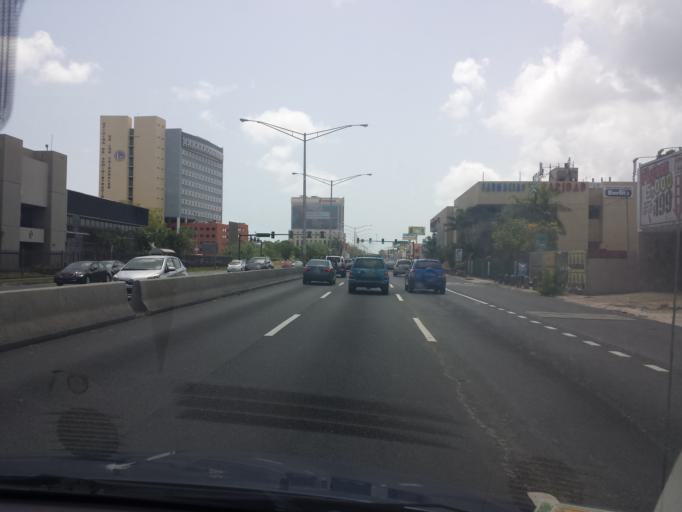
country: PR
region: Catano
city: Catano
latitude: 18.4074
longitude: -66.0665
